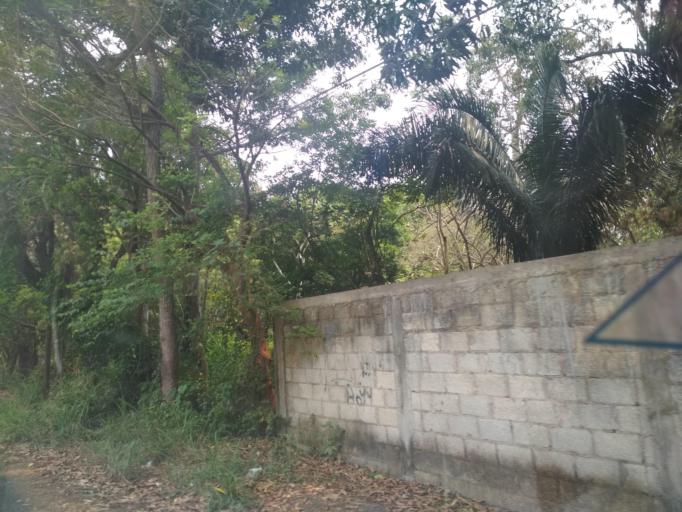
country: MX
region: Veracruz
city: El Tejar
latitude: 19.0525
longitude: -96.1539
